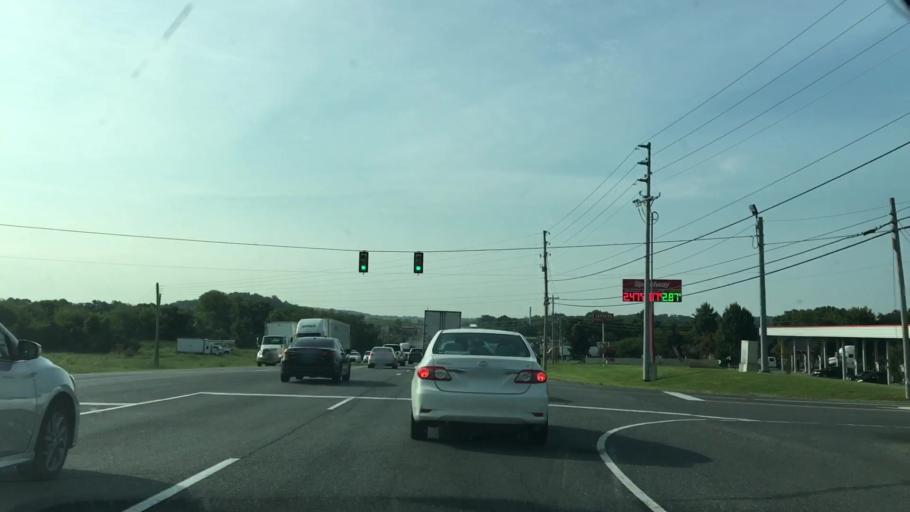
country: US
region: Tennessee
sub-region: Wilson County
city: Rural Hill
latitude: 36.1933
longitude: -86.4117
